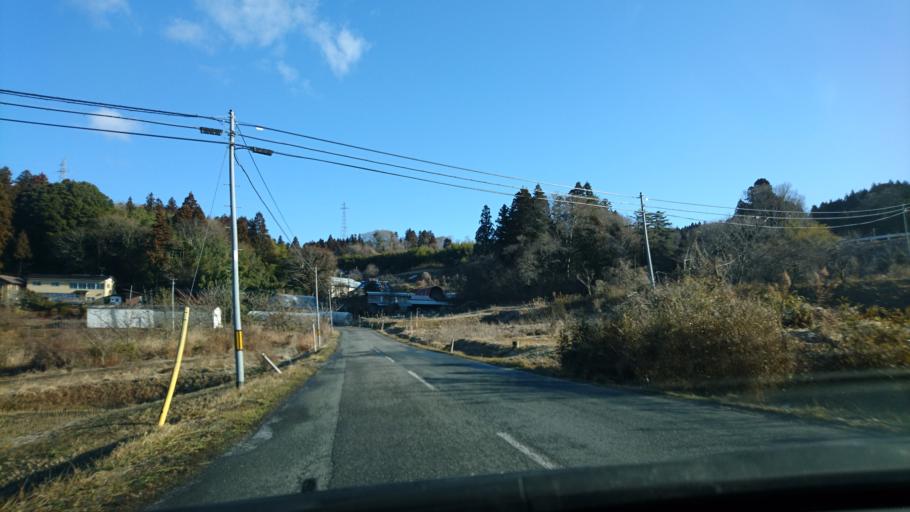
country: JP
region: Iwate
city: Ichinoseki
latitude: 38.8694
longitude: 141.2957
